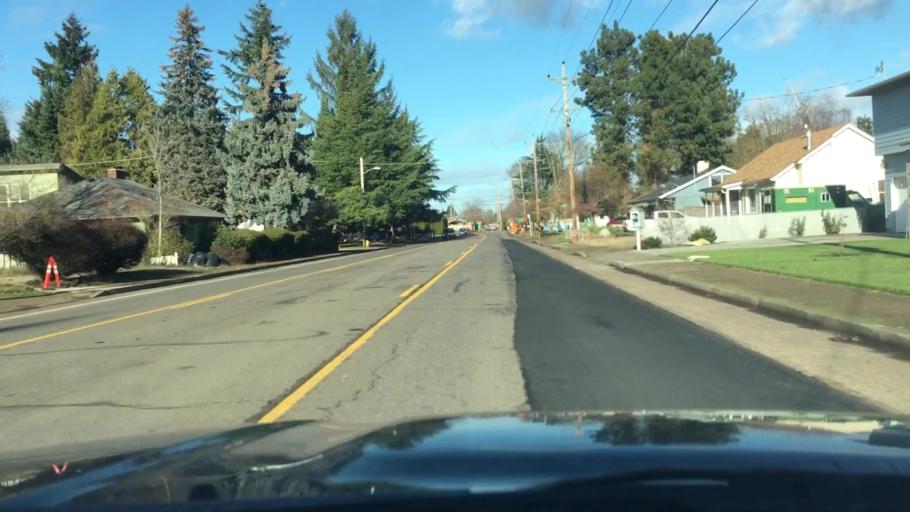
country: US
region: Oregon
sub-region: Lane County
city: Eugene
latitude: 44.0676
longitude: -123.1630
